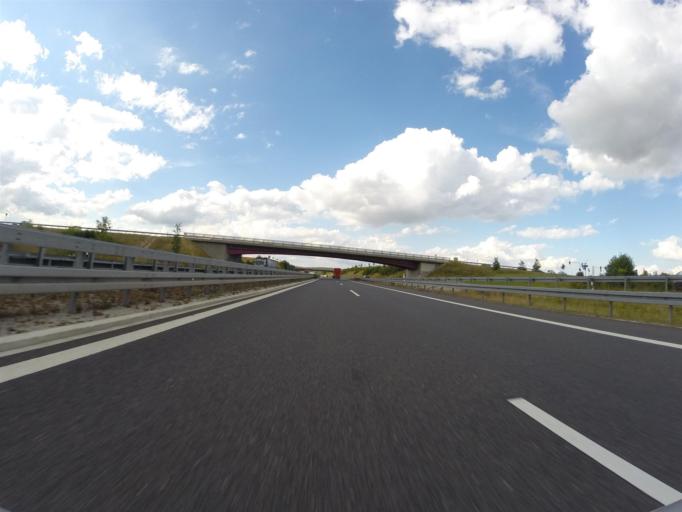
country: DE
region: Bavaria
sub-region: Upper Franconia
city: Niederfullbach
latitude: 50.2210
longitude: 11.0495
